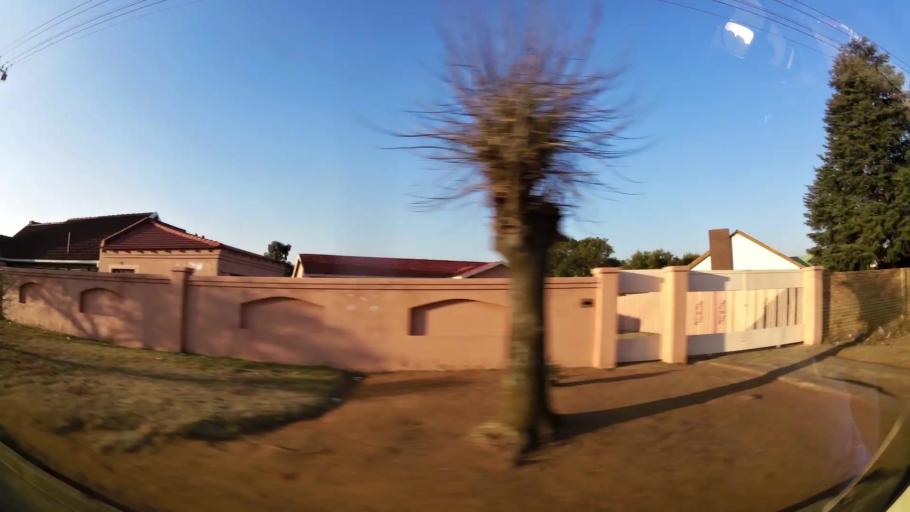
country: ZA
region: Gauteng
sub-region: West Rand District Municipality
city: Randfontein
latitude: -26.2088
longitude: 27.6559
